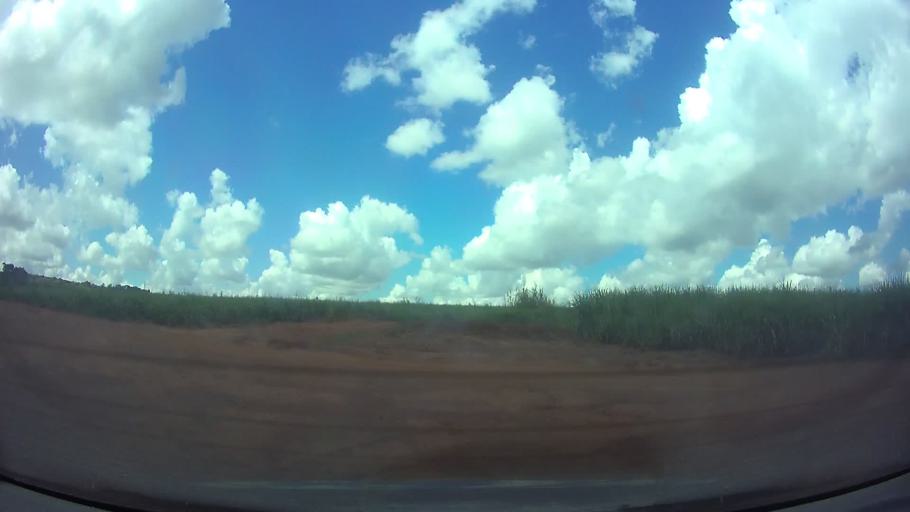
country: PY
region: Paraguari
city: La Colmena
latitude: -25.9518
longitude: -56.7673
